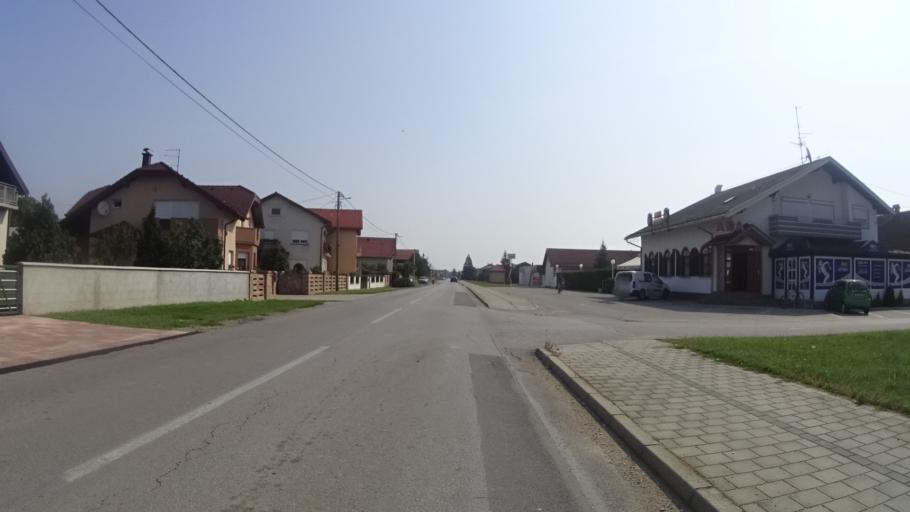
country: HR
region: Medimurska
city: Belica
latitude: 46.4007
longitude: 16.5000
